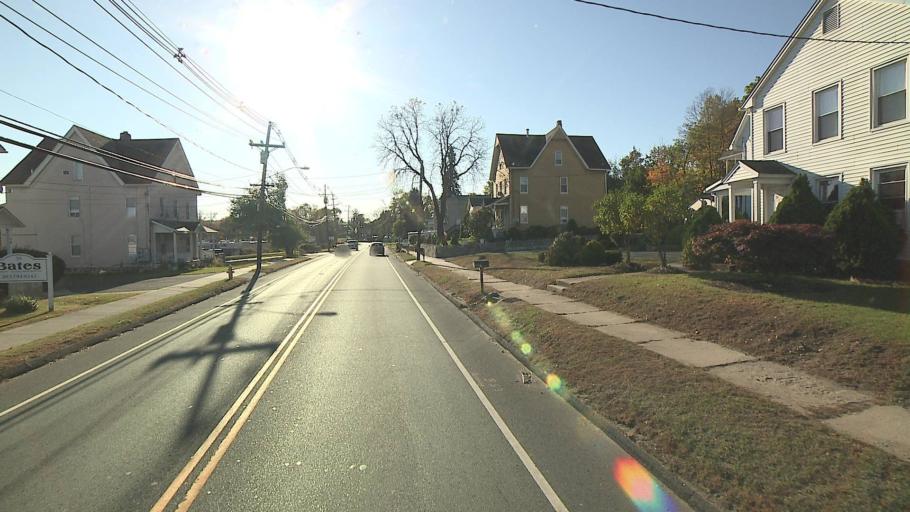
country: US
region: Connecticut
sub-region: Fairfield County
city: Danbury
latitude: 41.3878
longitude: -73.4322
